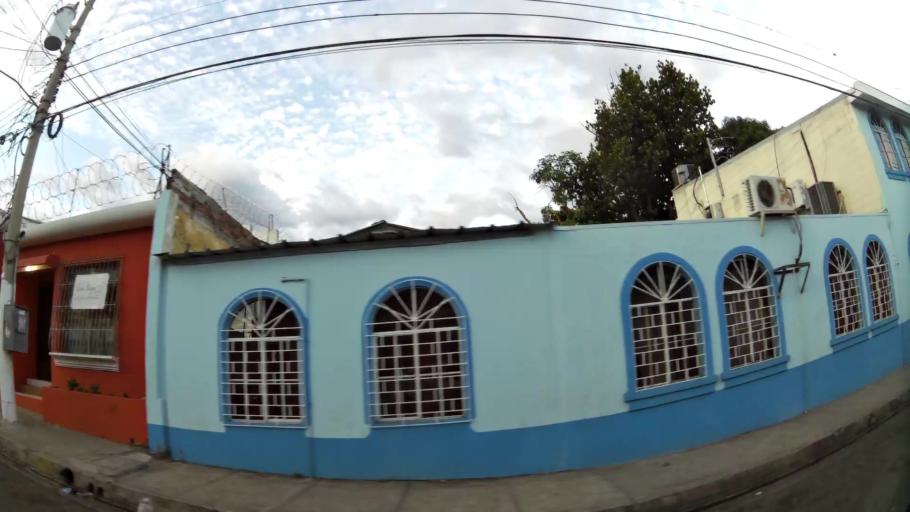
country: SV
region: San Vicente
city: San Vicente
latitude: 13.6453
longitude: -88.7857
